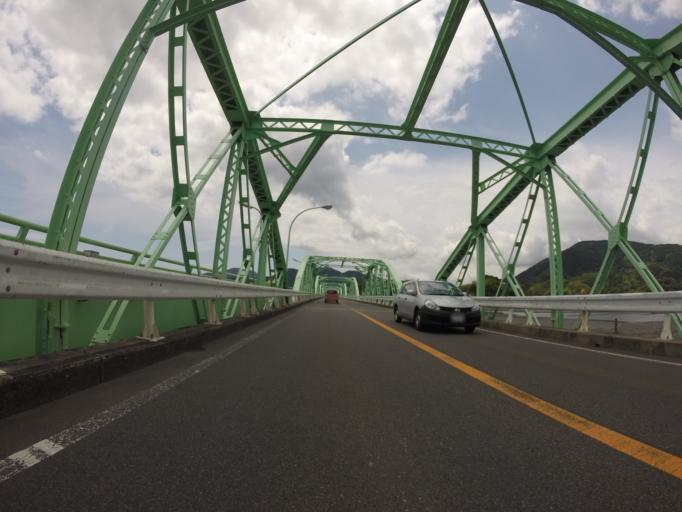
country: JP
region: Shizuoka
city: Shizuoka-shi
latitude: 34.9607
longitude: 138.3684
